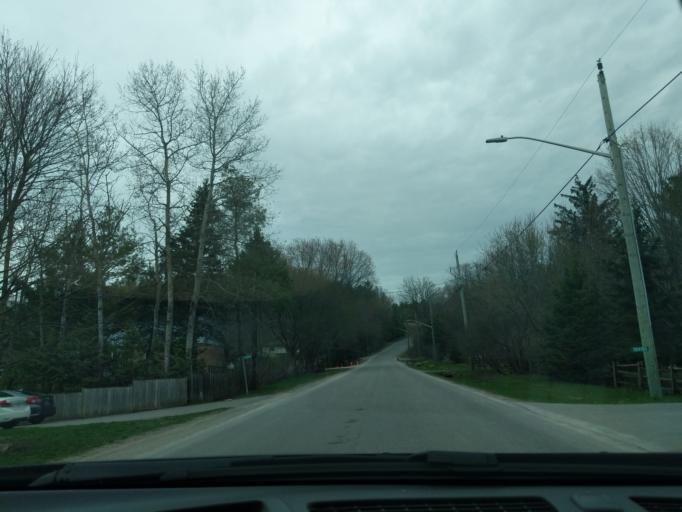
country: CA
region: Ontario
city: Orangeville
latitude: 44.0198
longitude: -79.9686
